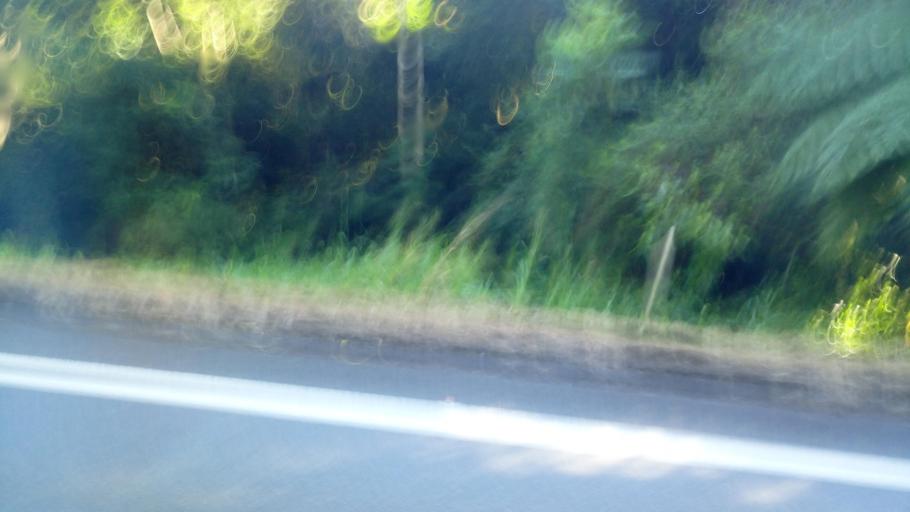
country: AU
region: Queensland
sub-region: Tablelands
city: Ravenshoe
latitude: -17.5950
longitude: 145.7445
